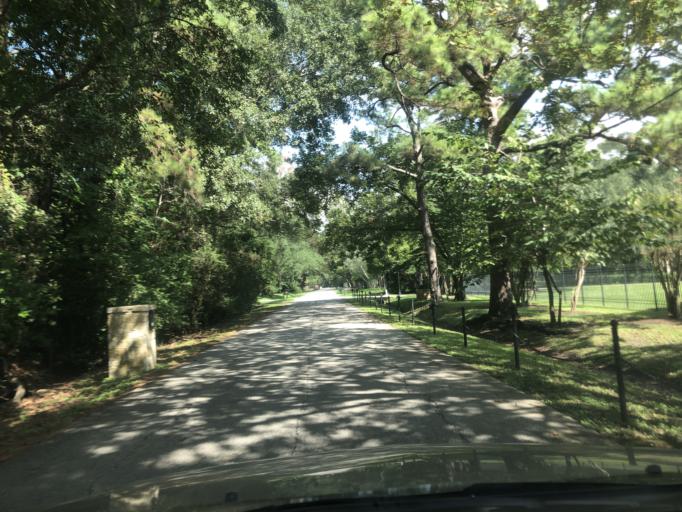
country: US
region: Texas
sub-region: Harris County
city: Bunker Hill Village
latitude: 29.7429
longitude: -95.5418
